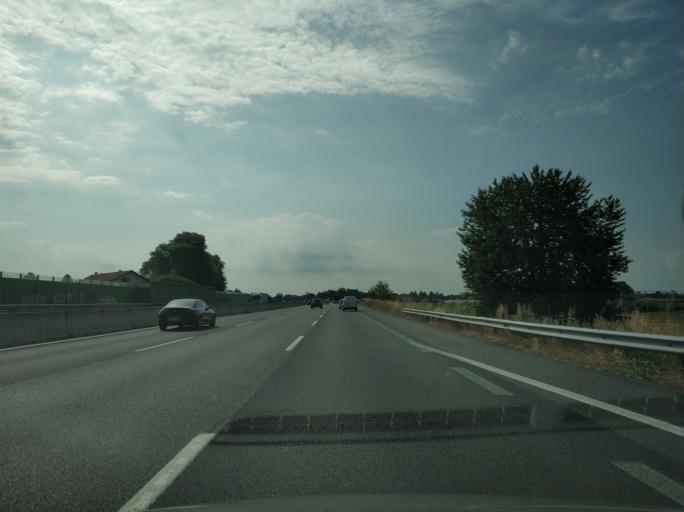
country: IT
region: Piedmont
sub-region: Provincia di Torino
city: Nichelino
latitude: 44.9802
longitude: 7.6477
